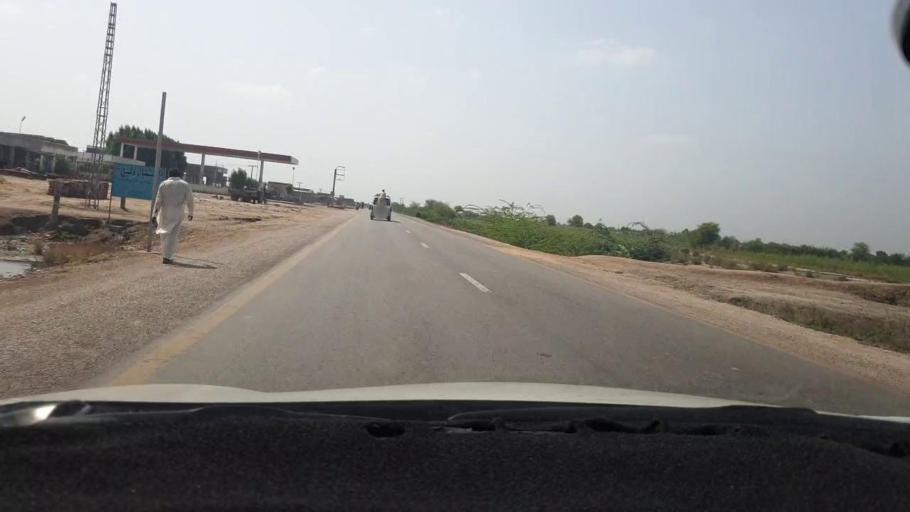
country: PK
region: Sindh
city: Mirpur Khas
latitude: 25.6103
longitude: 69.0830
